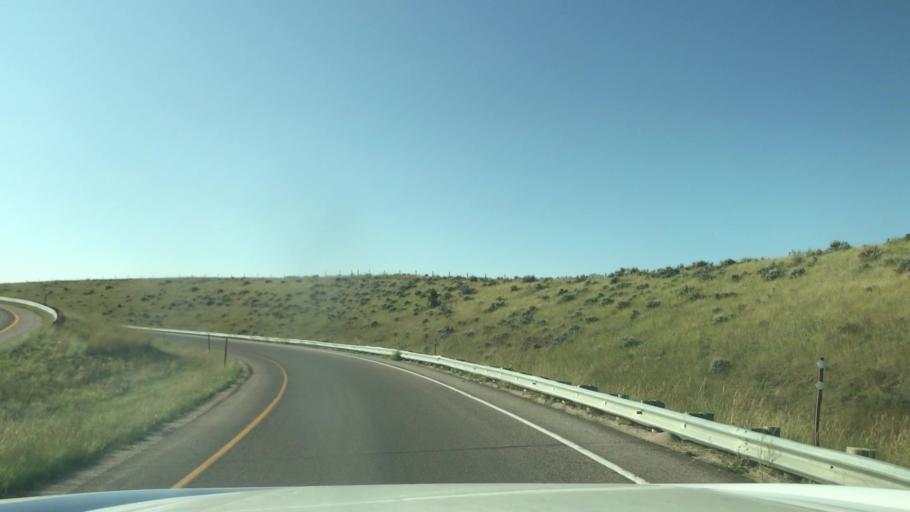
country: US
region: Wyoming
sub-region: Converse County
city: Douglas
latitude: 42.7306
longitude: -105.3412
